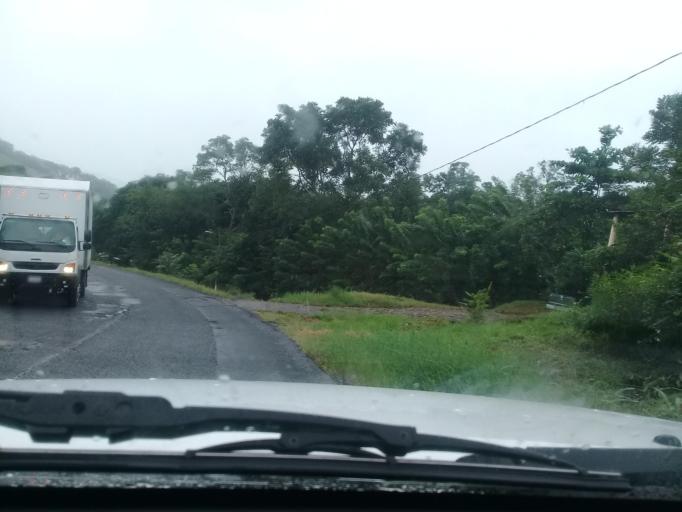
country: MX
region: Veracruz
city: Santiago Tuxtla
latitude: 18.4657
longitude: -95.2926
